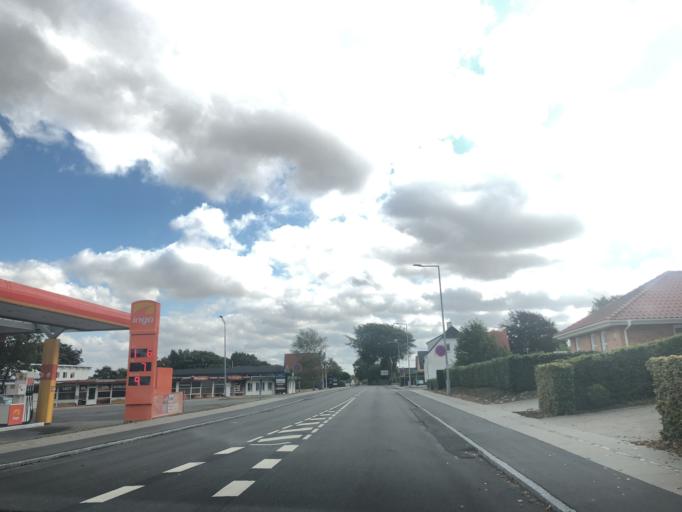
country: DK
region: Central Jutland
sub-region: Struer Kommune
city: Struer
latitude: 56.4797
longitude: 8.6049
